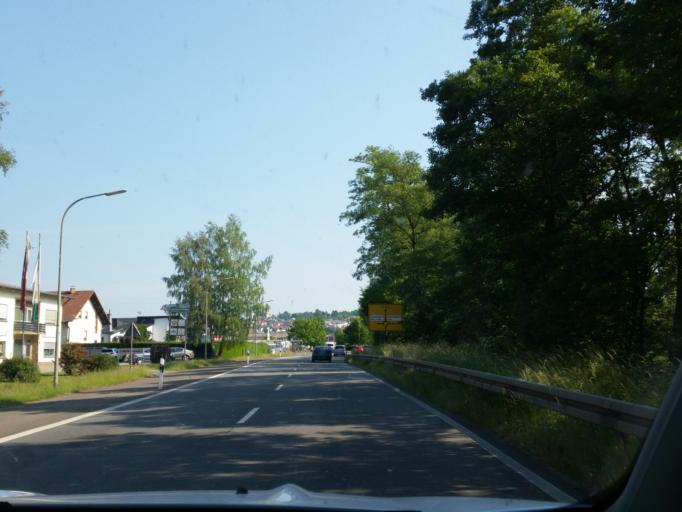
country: DE
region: Saarland
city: Schmelz
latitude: 49.4328
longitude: 6.8470
